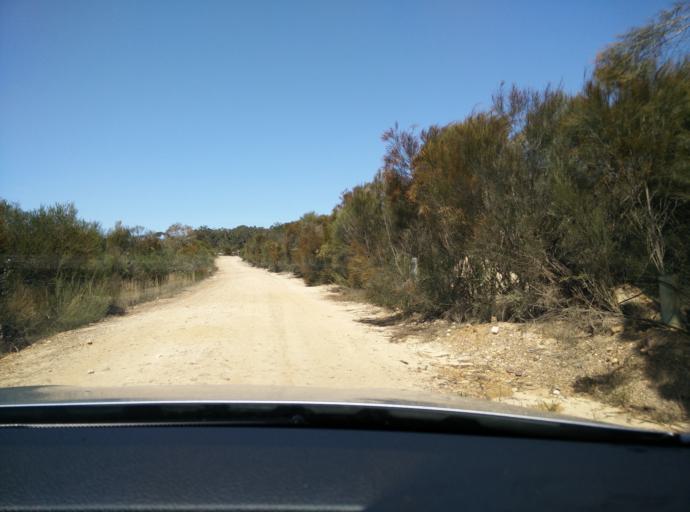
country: AU
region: New South Wales
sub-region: Gosford Shire
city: Umina
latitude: -33.5481
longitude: 151.2868
